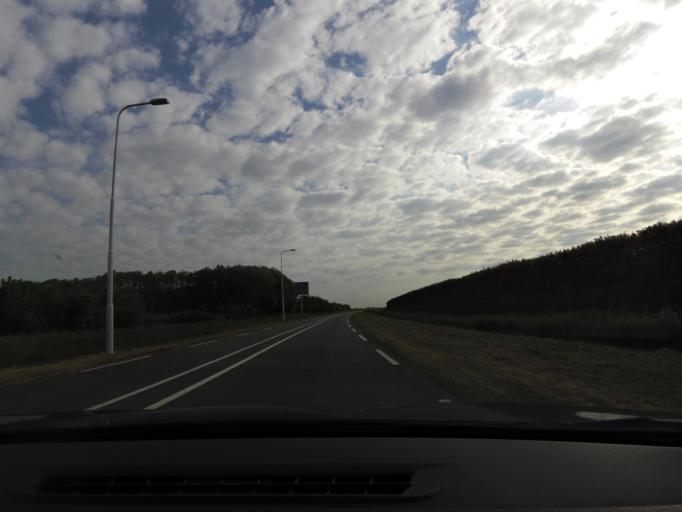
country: NL
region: Zeeland
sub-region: Schouwen-Duiveland
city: Haamstede
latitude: 51.7004
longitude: 3.7487
